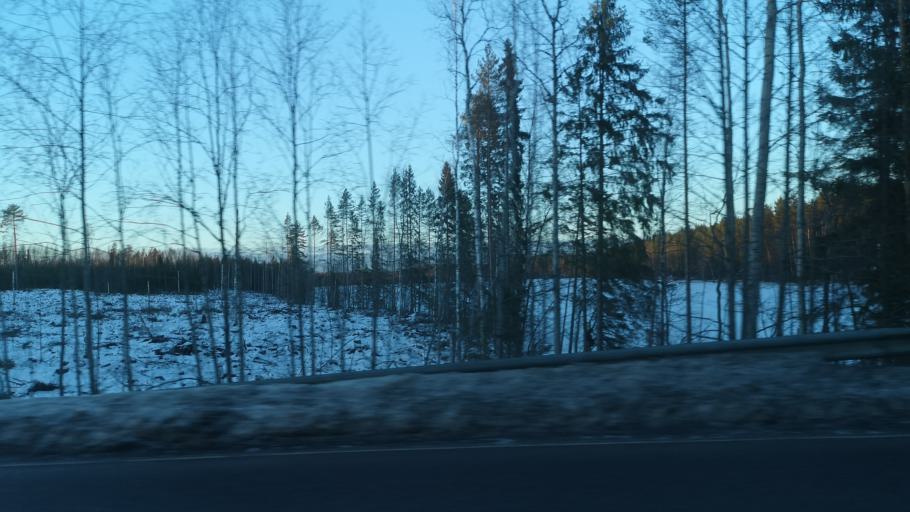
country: FI
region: Southern Savonia
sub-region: Pieksaemaeki
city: Juva
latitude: 61.9173
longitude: 28.0357
